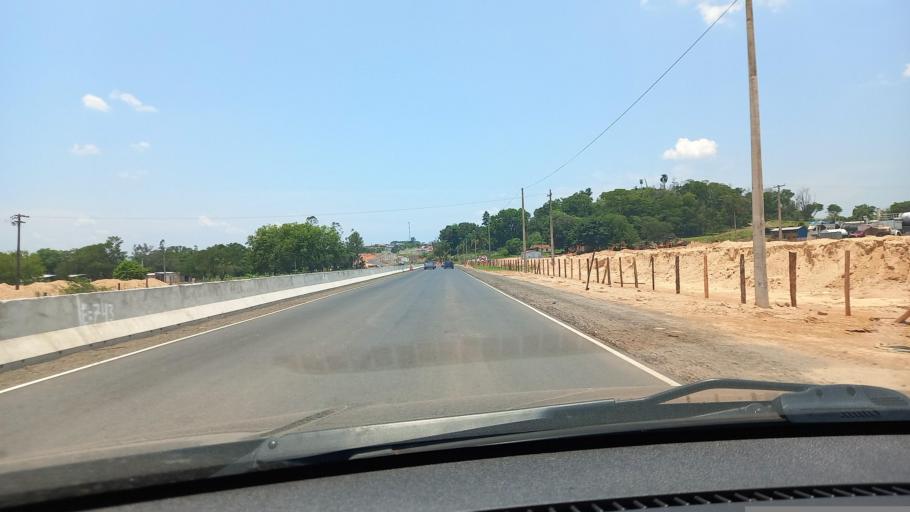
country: BR
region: Sao Paulo
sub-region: Itapira
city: Itapira
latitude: -22.4005
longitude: -46.8471
